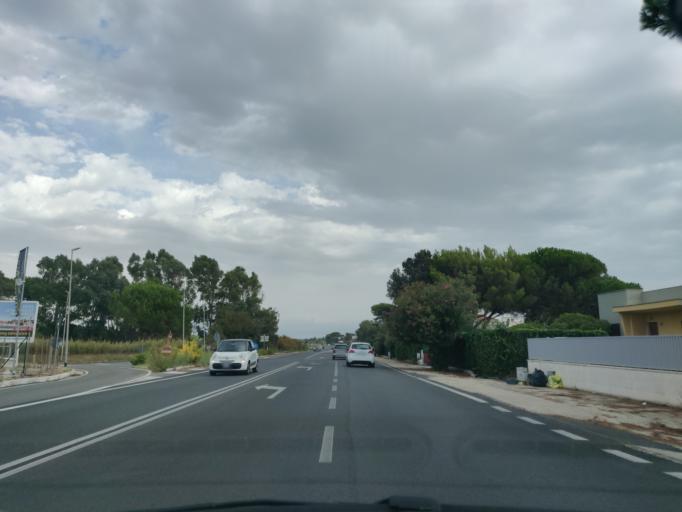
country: IT
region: Latium
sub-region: Citta metropolitana di Roma Capitale
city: Santa Marinella
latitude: 42.0389
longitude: 11.9176
